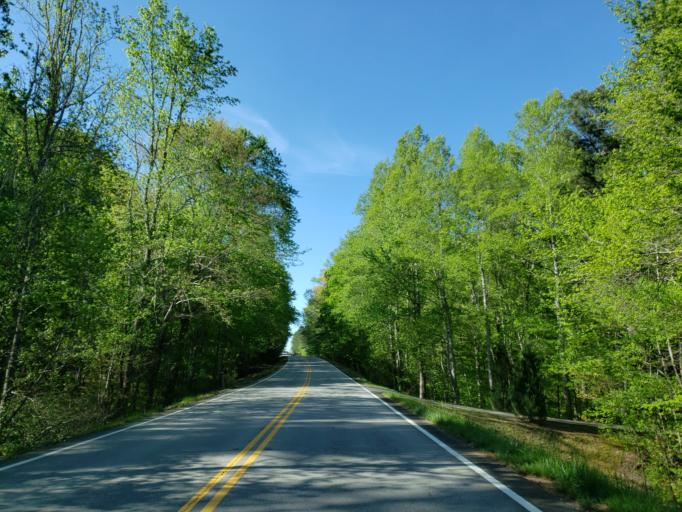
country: US
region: Georgia
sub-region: Haralson County
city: Tallapoosa
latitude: 33.8950
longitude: -85.3117
